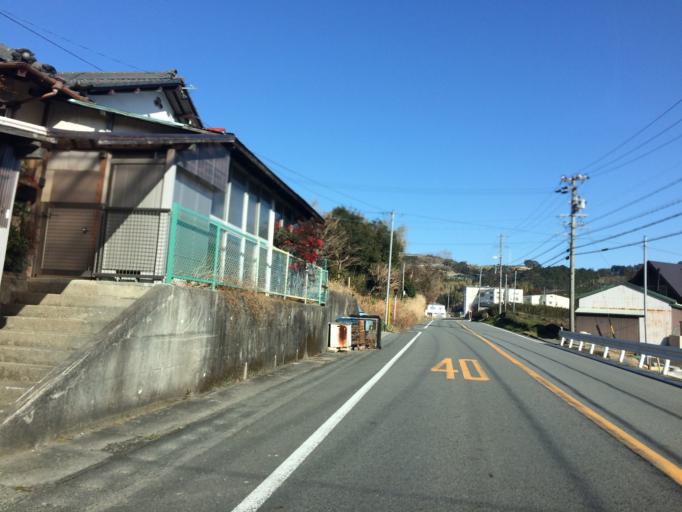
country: JP
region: Shizuoka
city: Shimada
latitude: 34.8496
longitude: 138.2029
